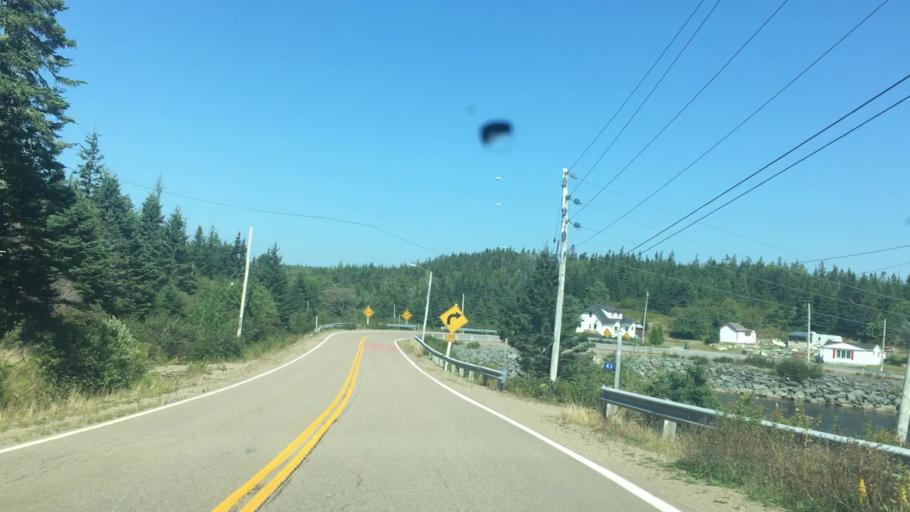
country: CA
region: Nova Scotia
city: Antigonish
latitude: 45.0268
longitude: -62.0308
